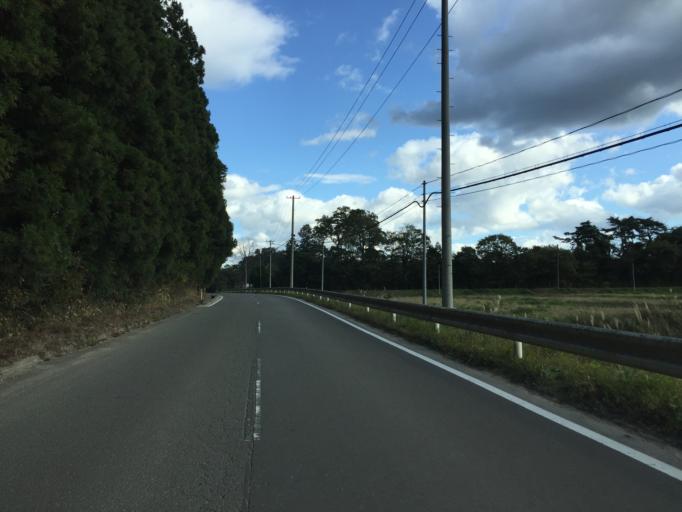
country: JP
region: Miyagi
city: Marumori
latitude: 37.8349
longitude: 140.8203
